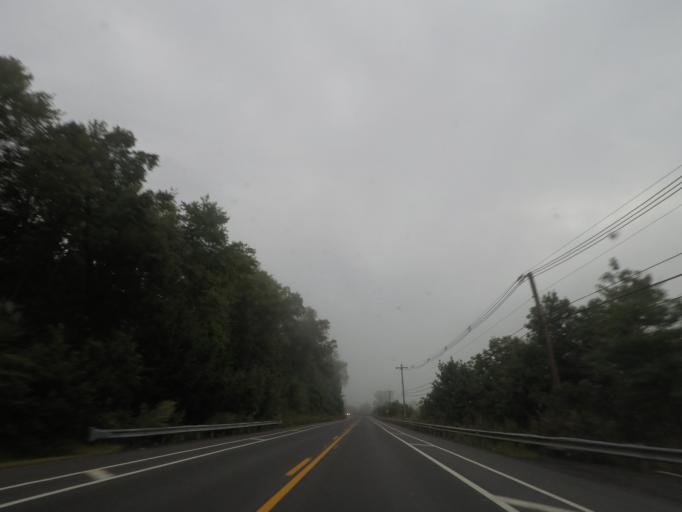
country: US
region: Massachusetts
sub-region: Hampden County
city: Palmer
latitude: 42.1453
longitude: -72.2773
